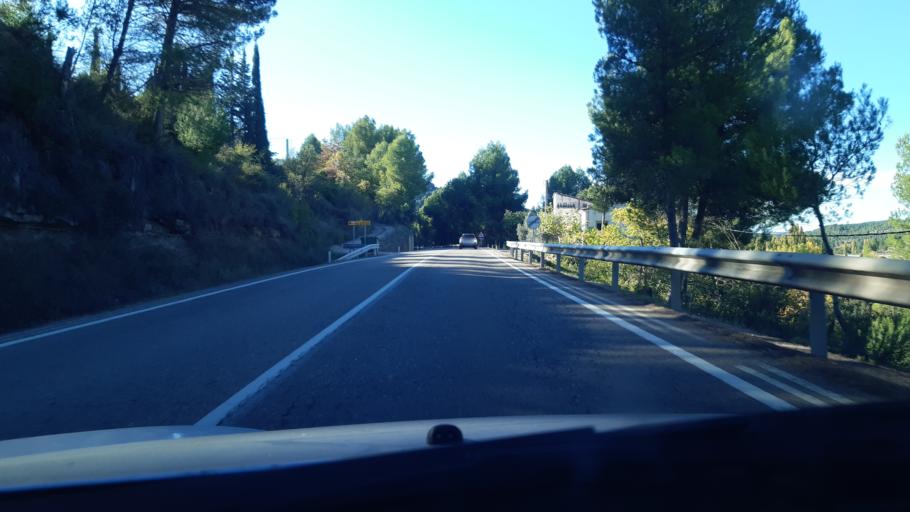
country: ES
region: Aragon
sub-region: Provincia de Teruel
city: Valderrobres
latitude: 40.8727
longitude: 0.1435
